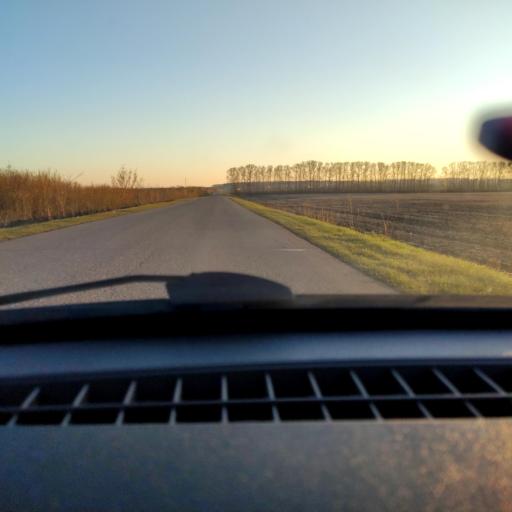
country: RU
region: Bashkortostan
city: Avdon
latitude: 54.5330
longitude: 55.6422
